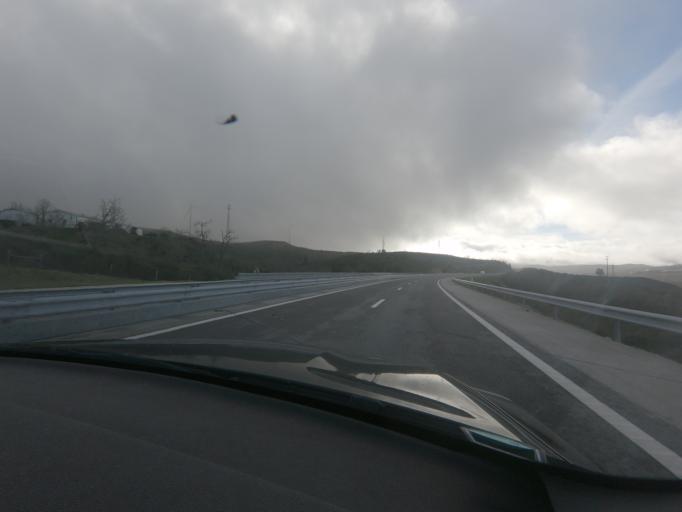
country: PT
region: Viseu
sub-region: Tarouca
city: Tarouca
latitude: 41.0217
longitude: -7.8758
